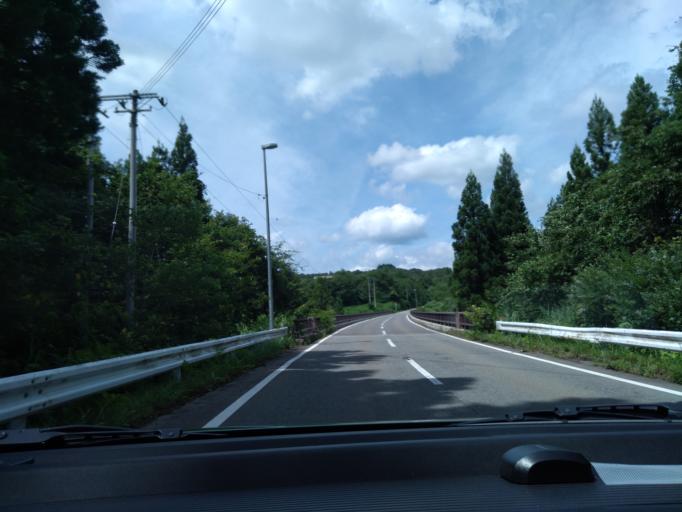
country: JP
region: Akita
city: Akita
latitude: 39.6765
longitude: 140.2893
